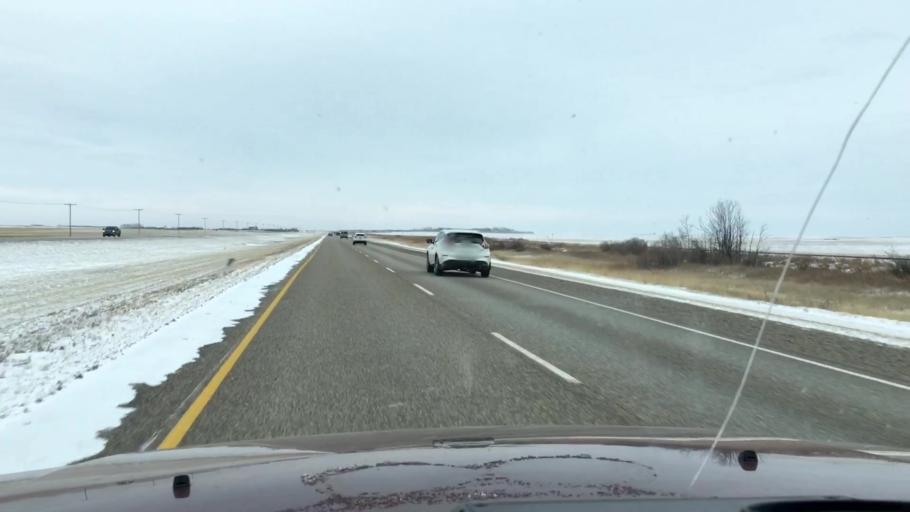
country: CA
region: Saskatchewan
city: Moose Jaw
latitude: 50.9940
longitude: -105.7568
